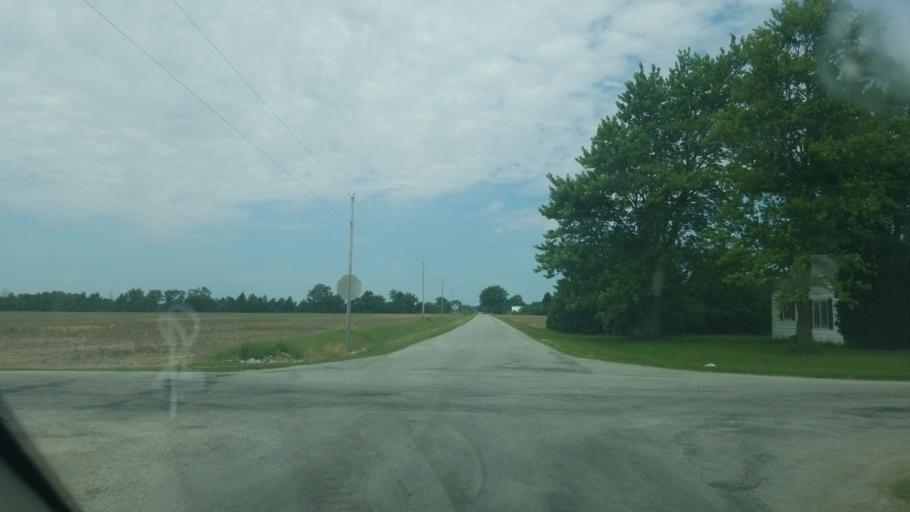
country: US
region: Ohio
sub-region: Wood County
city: North Baltimore
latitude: 41.2326
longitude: -83.5923
